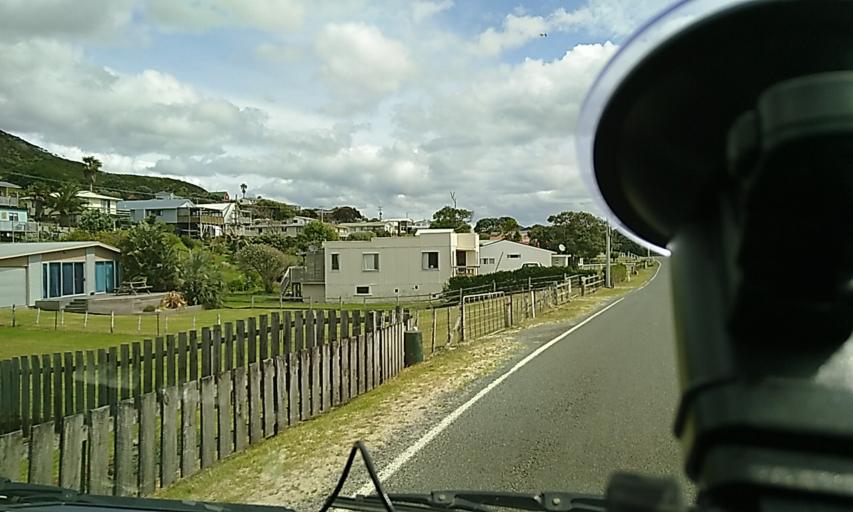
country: NZ
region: Northland
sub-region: Far North District
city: Ahipara
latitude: -35.5101
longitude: 173.3898
